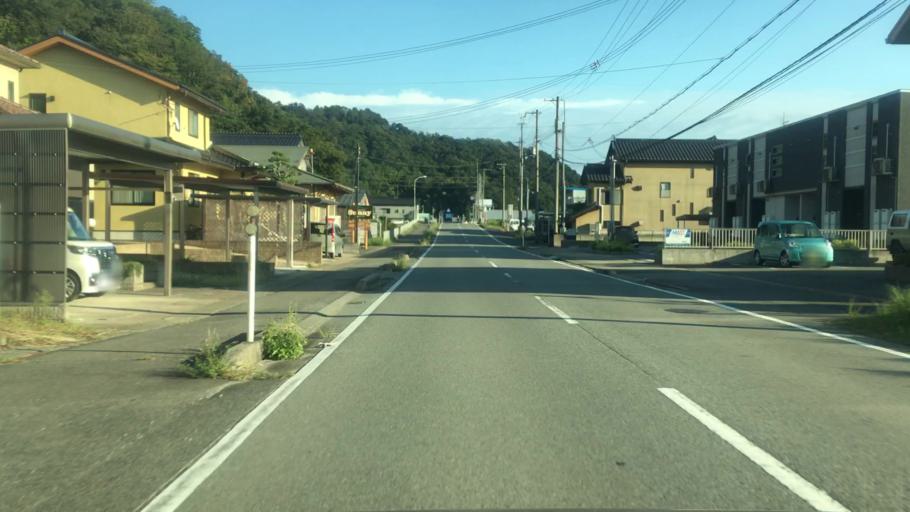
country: JP
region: Hyogo
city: Toyooka
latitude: 35.5618
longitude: 134.8221
